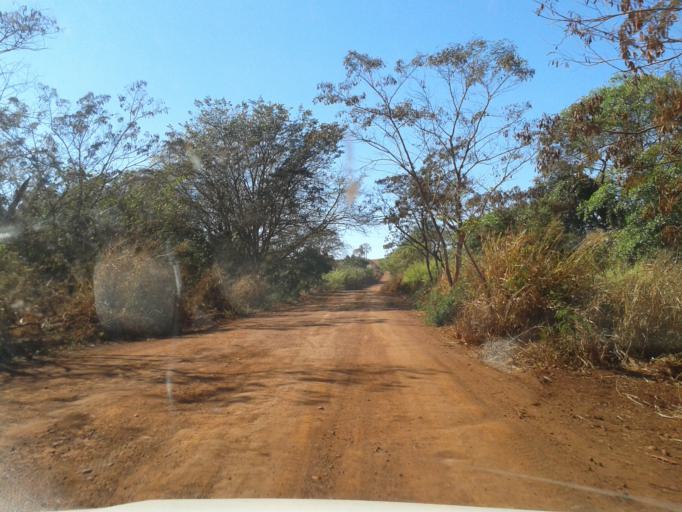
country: BR
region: Minas Gerais
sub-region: Centralina
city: Centralina
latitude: -18.5892
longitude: -49.1790
